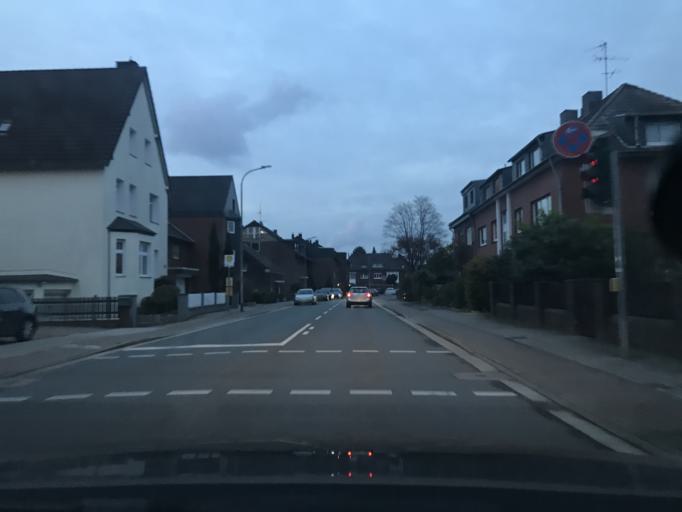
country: DE
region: North Rhine-Westphalia
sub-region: Regierungsbezirk Dusseldorf
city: Moers
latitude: 51.4438
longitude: 6.6253
